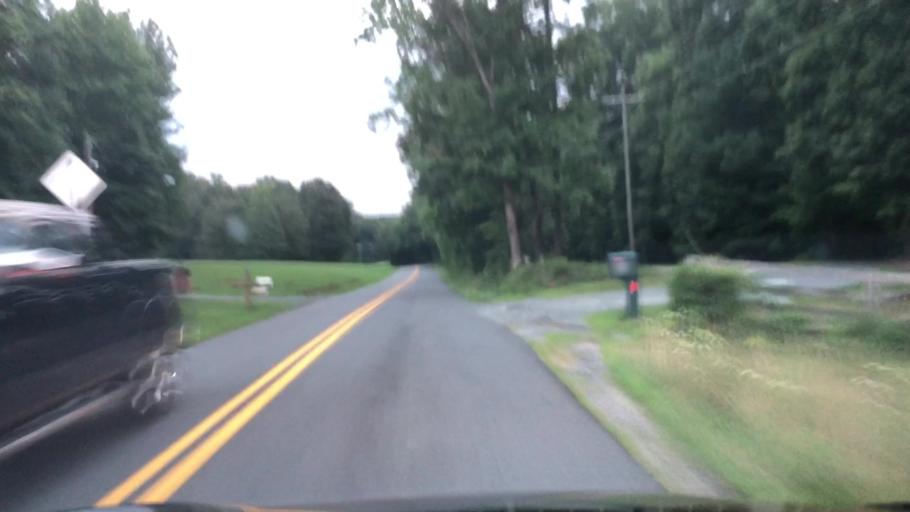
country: US
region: Virginia
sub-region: Stafford County
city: Falmouth
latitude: 38.4379
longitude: -77.5877
